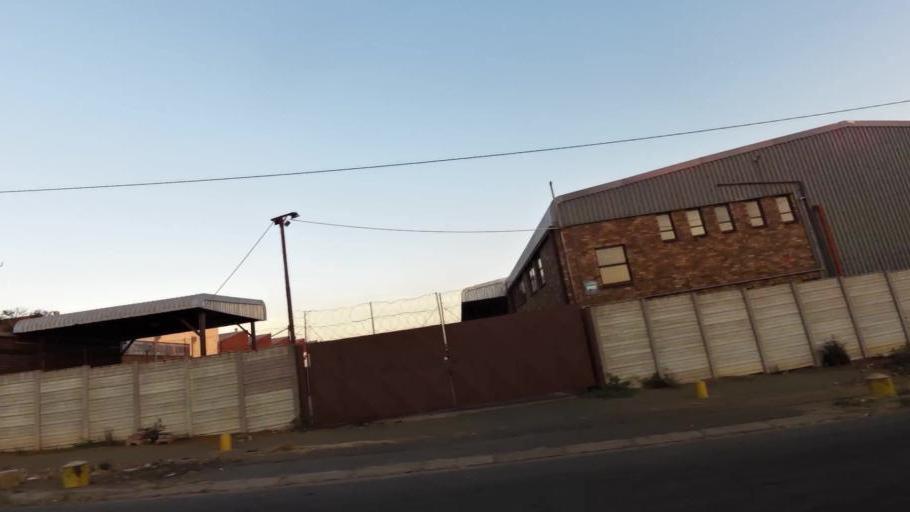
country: ZA
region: Gauteng
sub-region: City of Johannesburg Metropolitan Municipality
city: Johannesburg
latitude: -26.1989
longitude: 27.9776
